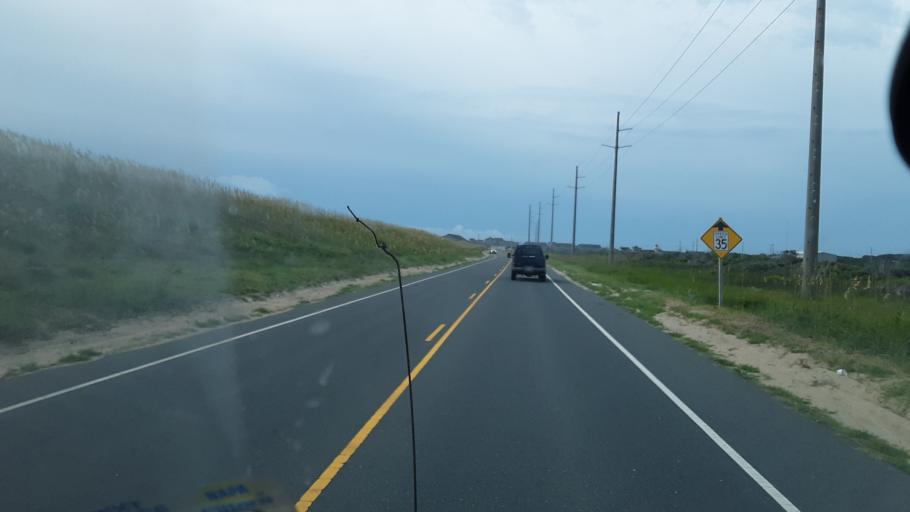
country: US
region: North Carolina
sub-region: Dare County
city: Buxton
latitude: 35.2725
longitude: -75.5187
